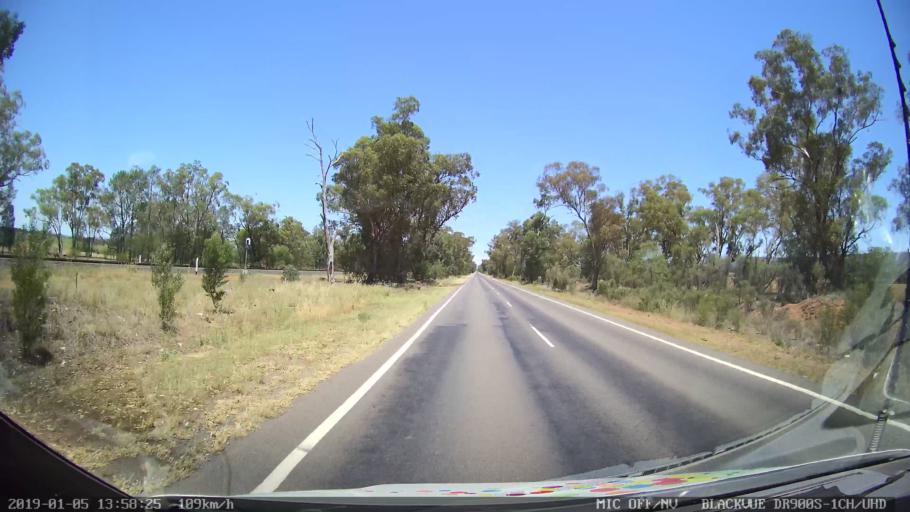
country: AU
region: New South Wales
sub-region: Gunnedah
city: Gunnedah
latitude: -31.1387
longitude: 150.2853
